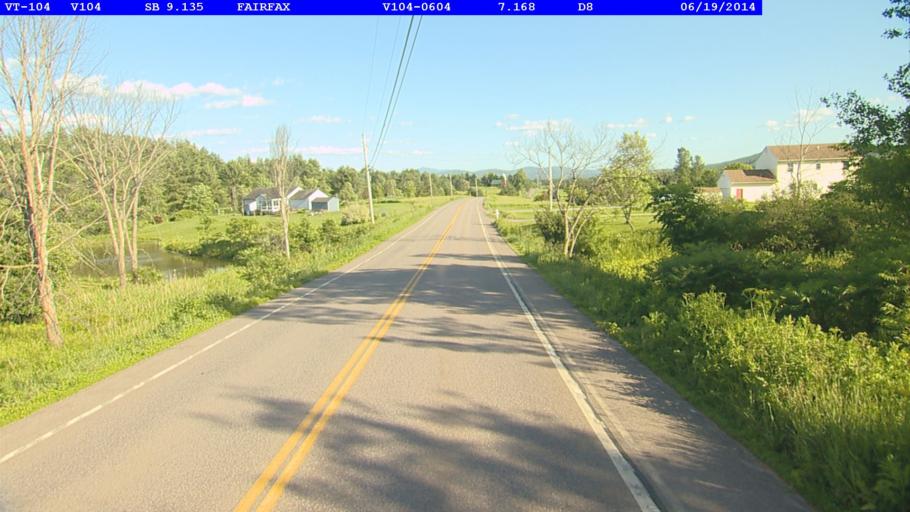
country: US
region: Vermont
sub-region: Chittenden County
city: Milton
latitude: 44.6885
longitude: -73.0322
